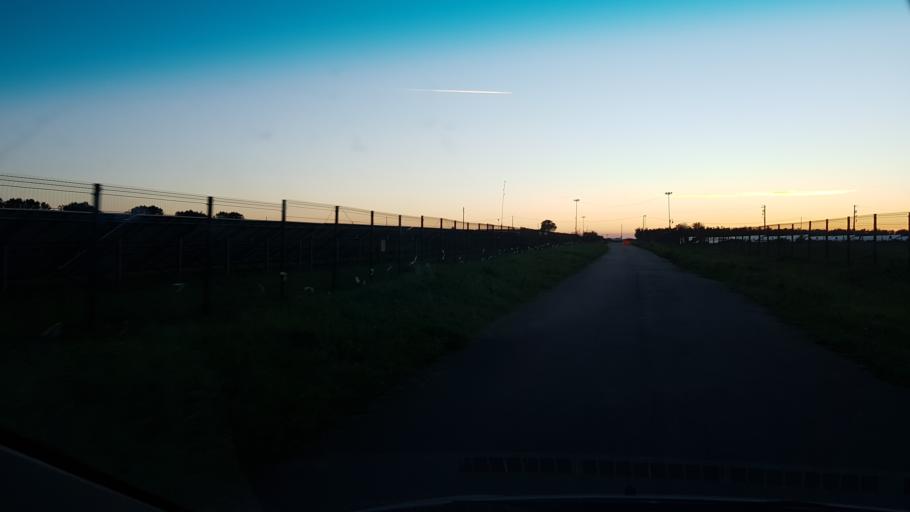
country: IT
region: Apulia
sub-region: Provincia di Brindisi
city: San Pietro Vernotico
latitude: 40.5075
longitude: 17.9679
